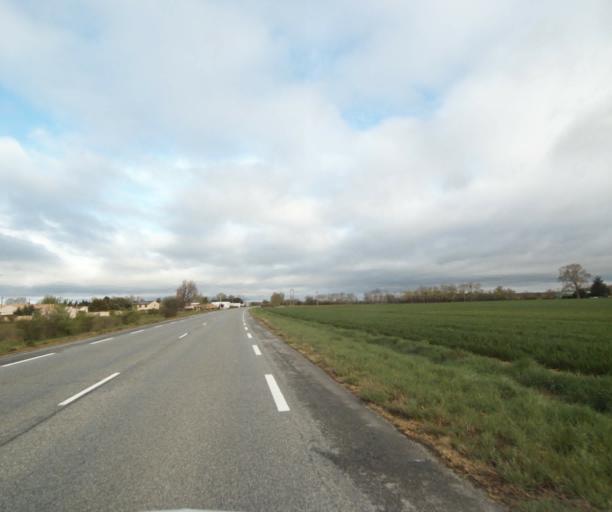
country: FR
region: Midi-Pyrenees
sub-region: Departement de l'Ariege
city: Saverdun
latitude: 43.2448
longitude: 1.5756
